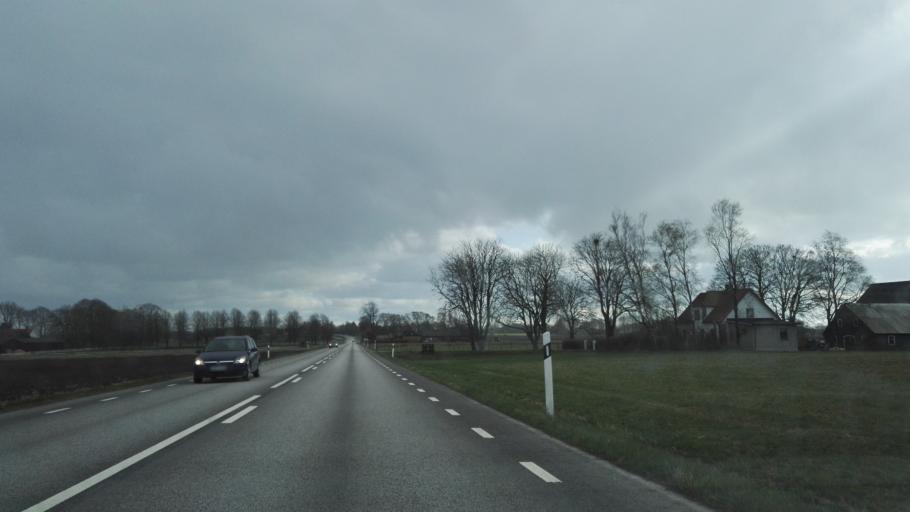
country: SE
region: Skane
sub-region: Horby Kommun
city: Hoerby
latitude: 55.7752
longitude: 13.6741
